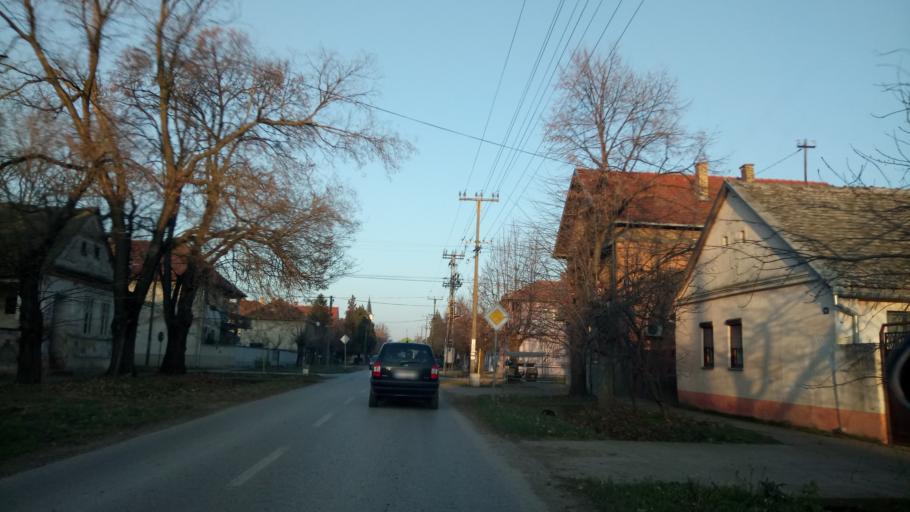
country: RS
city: Novi Slankamen
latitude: 45.1213
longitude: 20.2332
